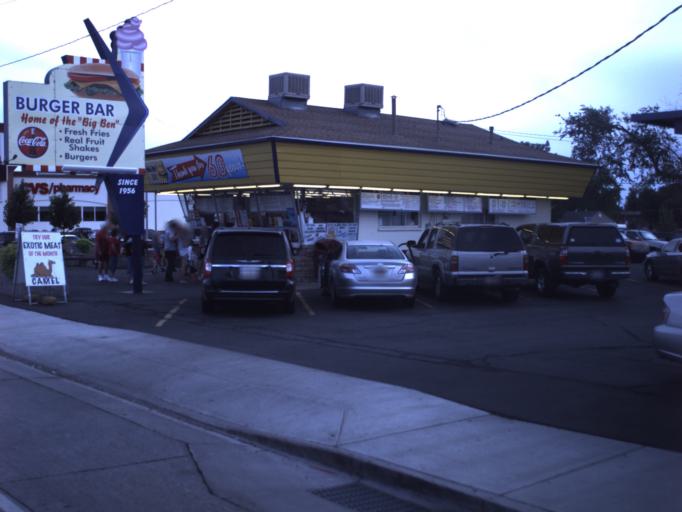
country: US
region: Utah
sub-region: Weber County
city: Roy
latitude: 41.1678
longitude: -112.0261
